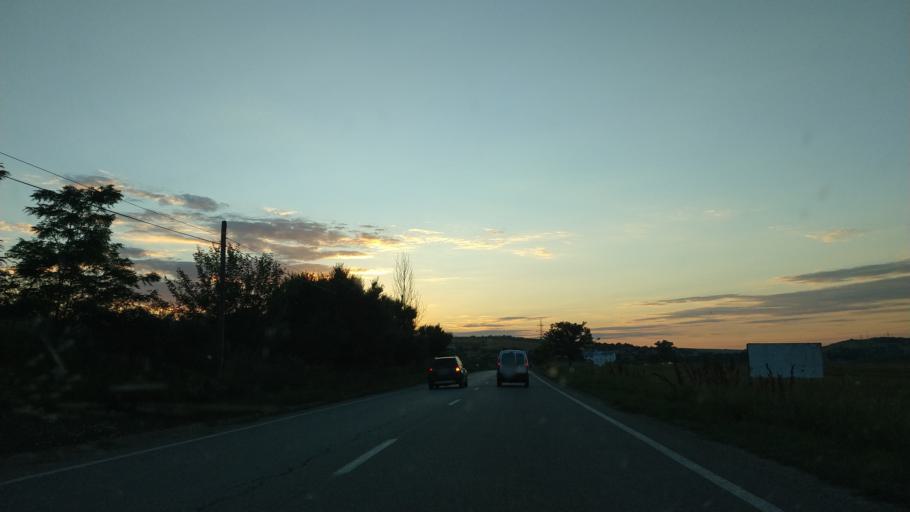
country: RO
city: Vanatori
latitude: 47.2259
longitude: 27.5413
